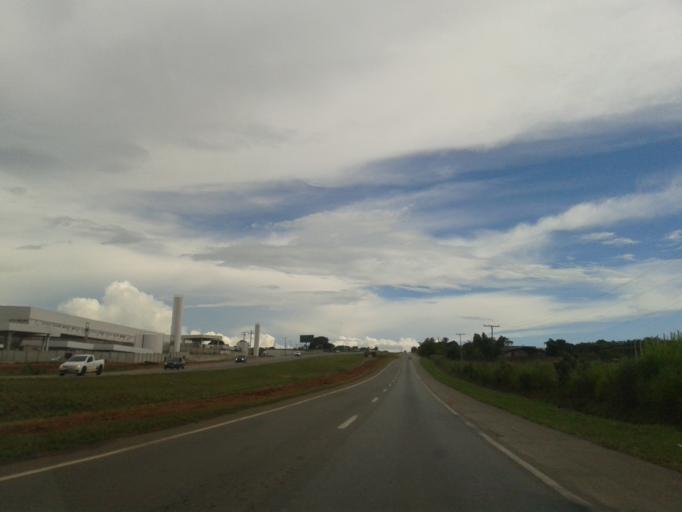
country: BR
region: Goias
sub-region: Aparecida De Goiania
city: Aparecida de Goiania
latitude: -16.8715
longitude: -49.2514
